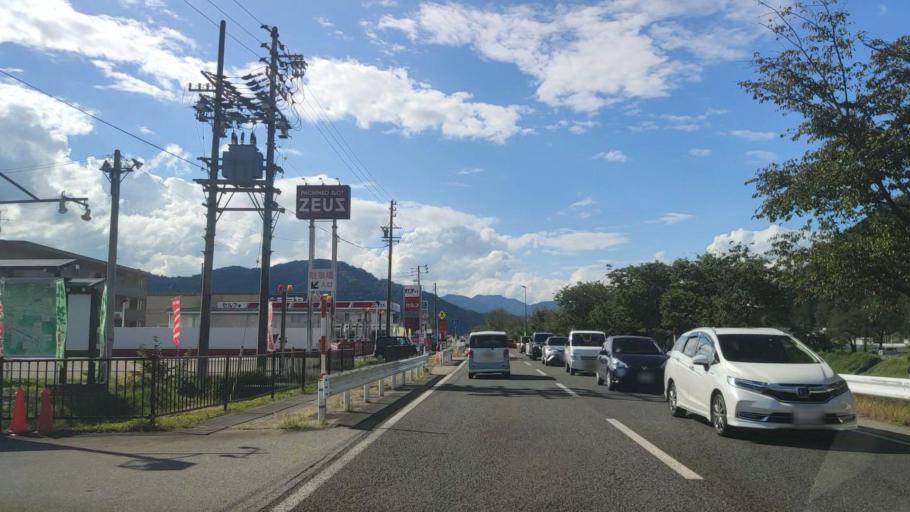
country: JP
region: Gifu
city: Takayama
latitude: 36.2050
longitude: 137.2248
